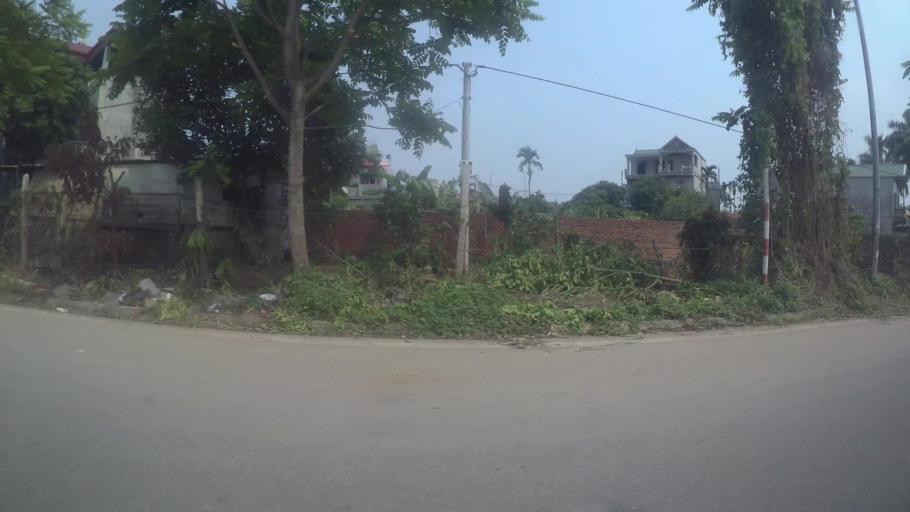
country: VN
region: Ha Noi
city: Quoc Oai
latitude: 20.9944
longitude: 105.5869
